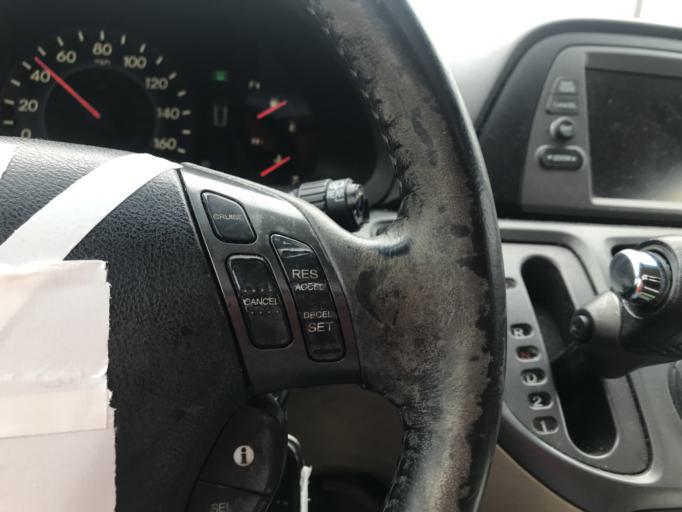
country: US
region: Louisiana
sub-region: Orleans Parish
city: New Orleans
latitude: 29.9535
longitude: -90.0835
